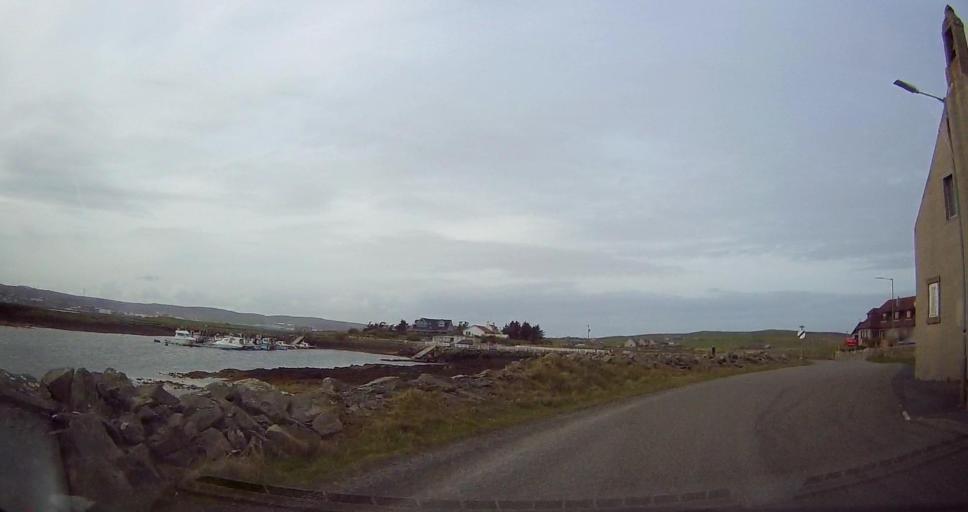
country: GB
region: Scotland
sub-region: Shetland Islands
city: Shetland
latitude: 60.1503
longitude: -1.1138
